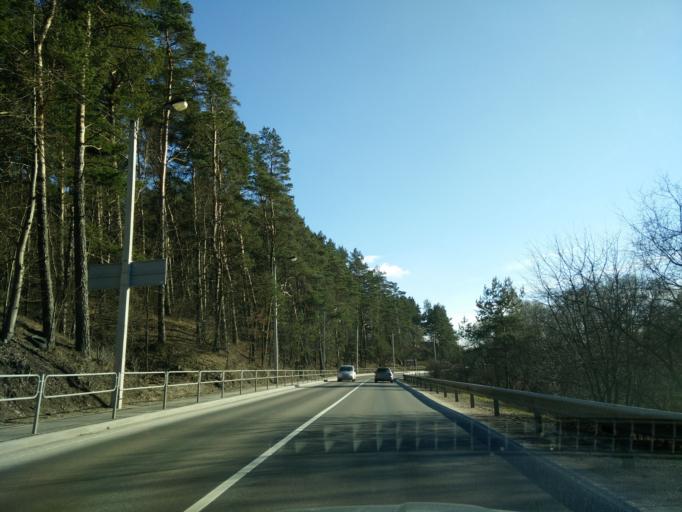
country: LT
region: Kauno apskritis
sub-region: Kauno rajonas
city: Akademija (Kaunas)
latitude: 54.9271
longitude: 23.7931
